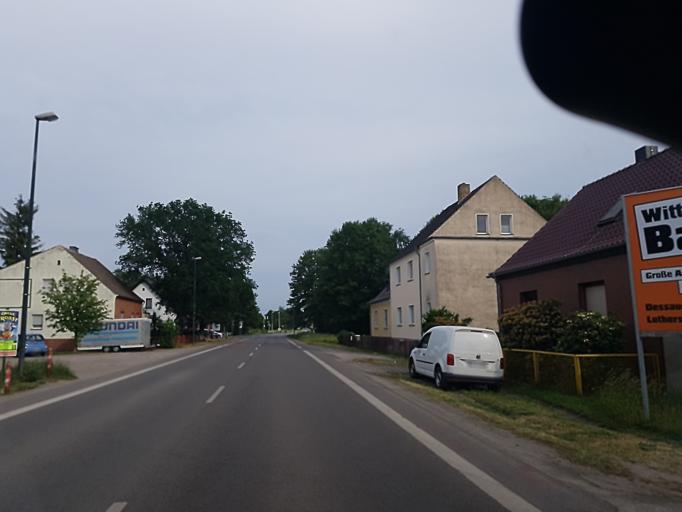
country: DE
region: Saxony-Anhalt
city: Wittenburg
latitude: 51.8711
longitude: 12.6729
